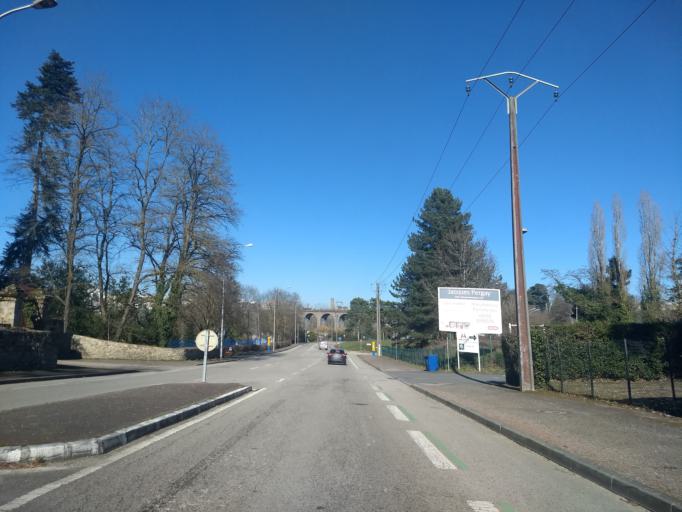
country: FR
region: Limousin
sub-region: Departement de la Haute-Vienne
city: Limoges
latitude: 45.8144
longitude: 1.2592
